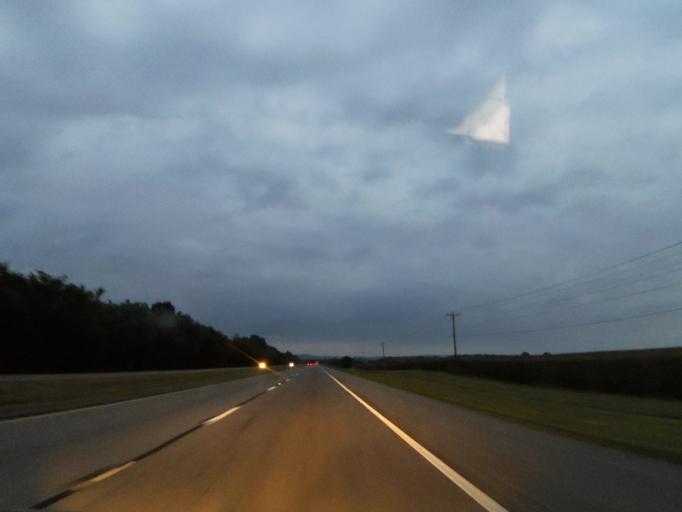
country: US
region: Alabama
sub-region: Madison County
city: New Hope
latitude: 34.6366
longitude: -86.3174
